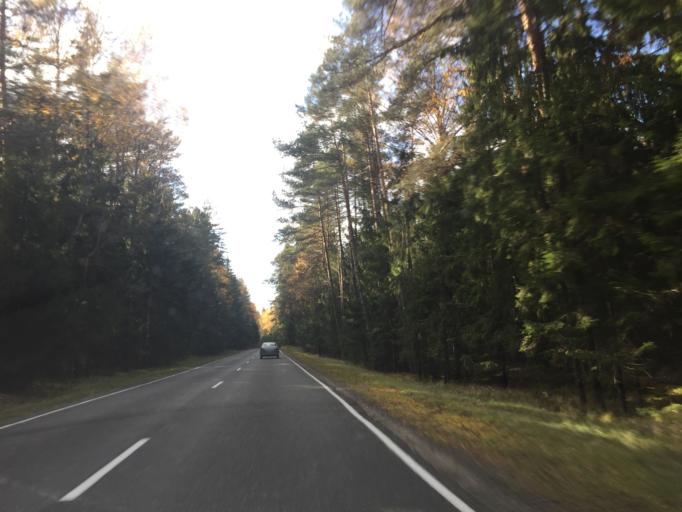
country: BY
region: Minsk
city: Narach
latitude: 54.9412
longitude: 26.5708
